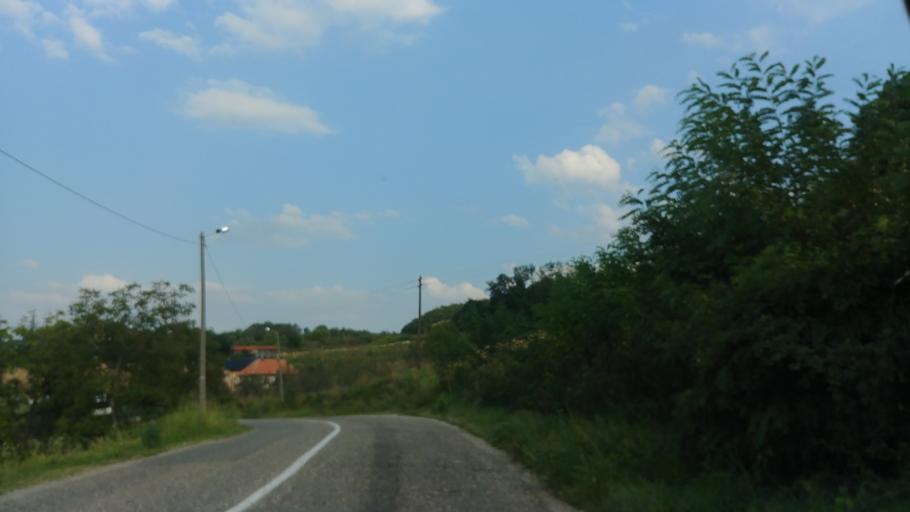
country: BA
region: Republika Srpska
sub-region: Opstina Ugljevik
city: Ugljevik
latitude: 44.7072
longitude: 18.9497
